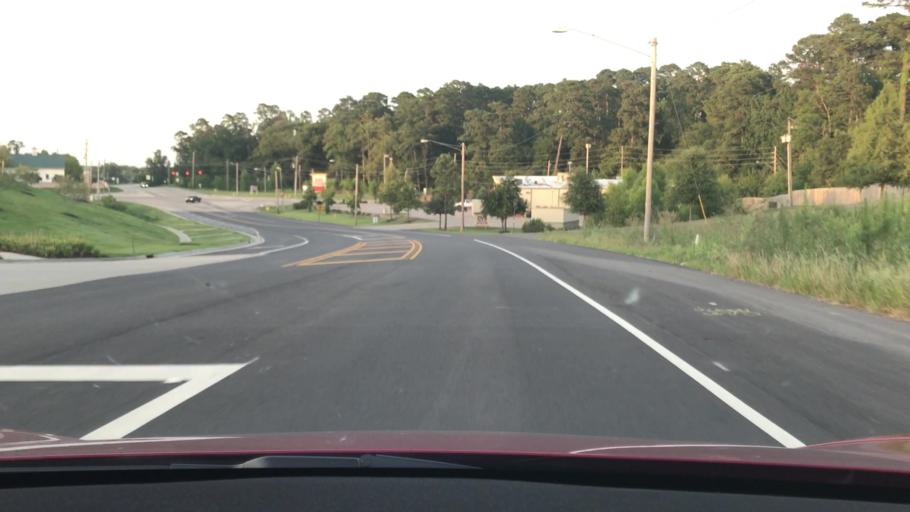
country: US
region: Louisiana
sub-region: Bossier Parish
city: Bossier City
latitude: 32.3931
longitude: -93.7271
